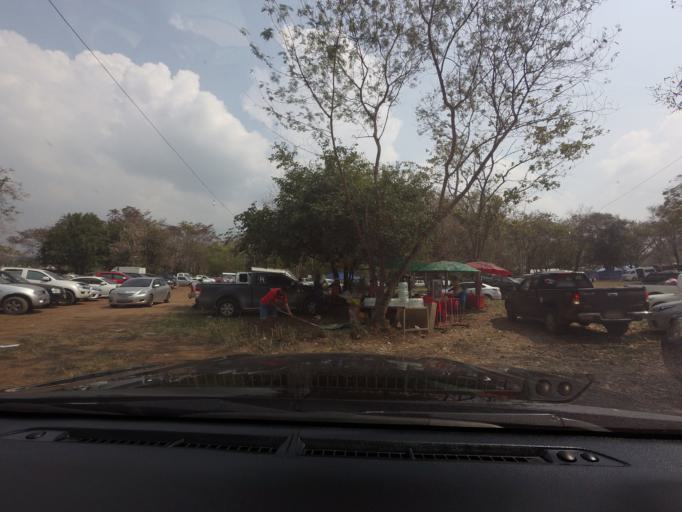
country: TH
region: Sara Buri
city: Muak Lek
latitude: 14.6344
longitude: 101.1923
